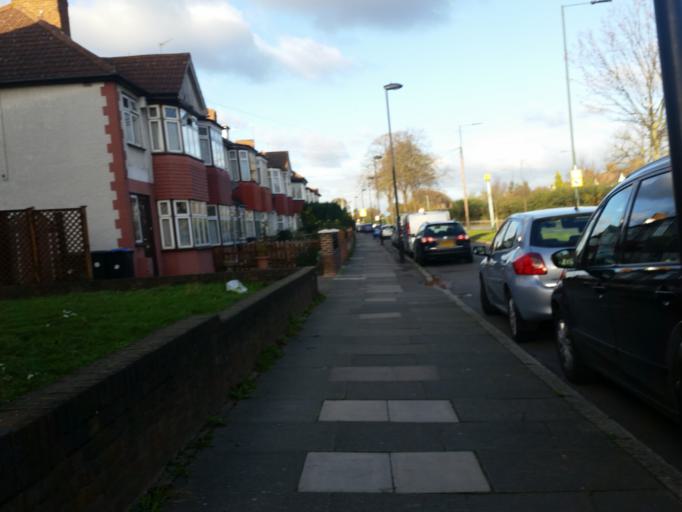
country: GB
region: England
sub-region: Greater London
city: Enfield
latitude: 51.6228
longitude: -0.0824
